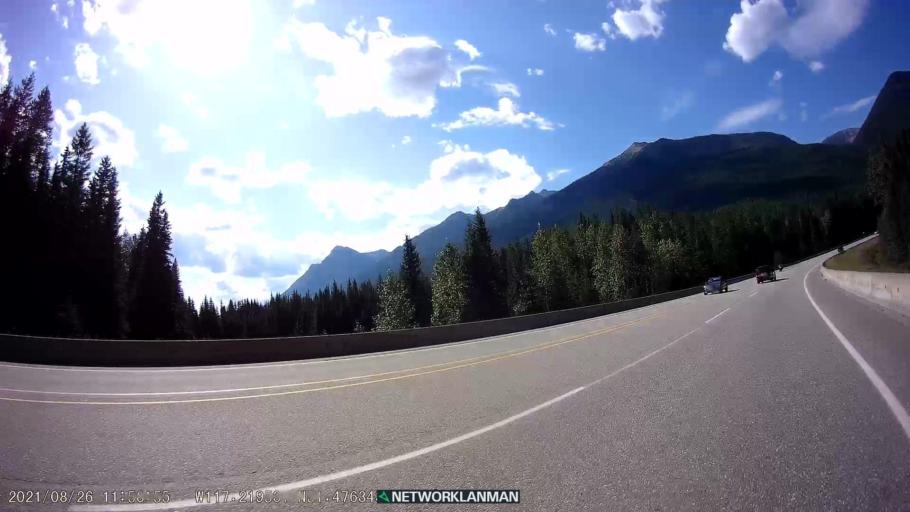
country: CA
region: British Columbia
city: Golden
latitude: 51.4764
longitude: -117.2208
